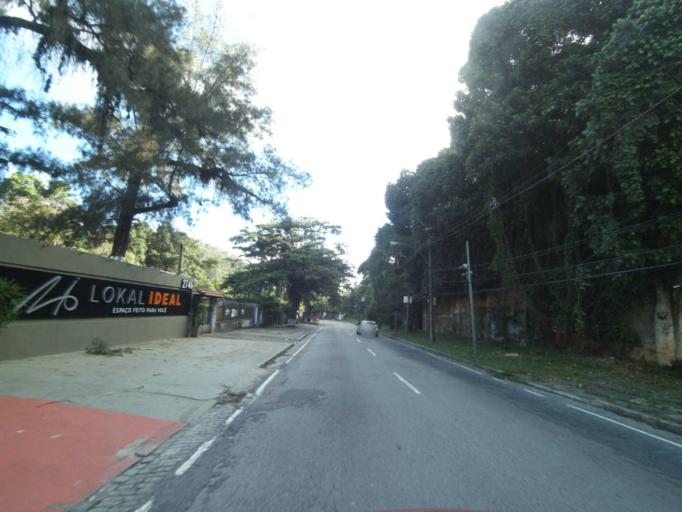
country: BR
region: Rio de Janeiro
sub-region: Rio De Janeiro
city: Rio de Janeiro
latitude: -22.9279
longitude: -43.3207
